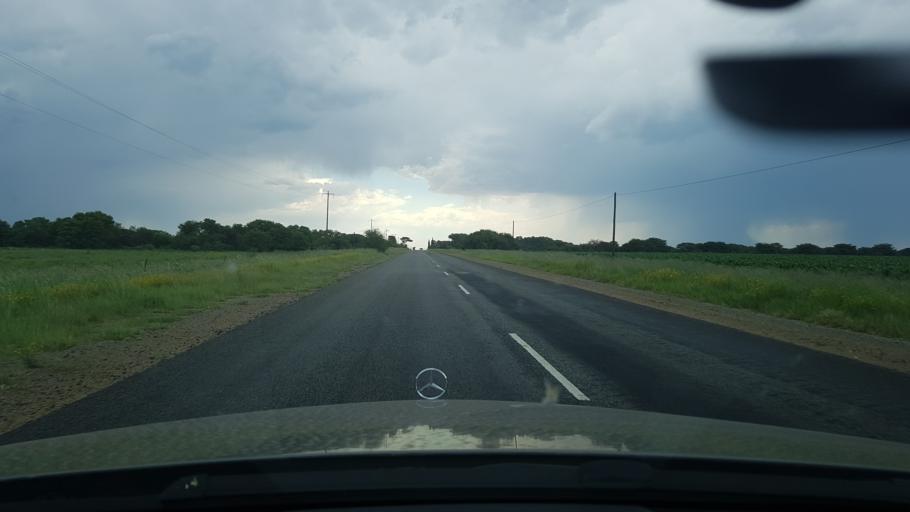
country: ZA
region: Orange Free State
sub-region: Lejweleputswa District Municipality
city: Hoopstad
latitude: -27.9847
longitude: 25.6586
